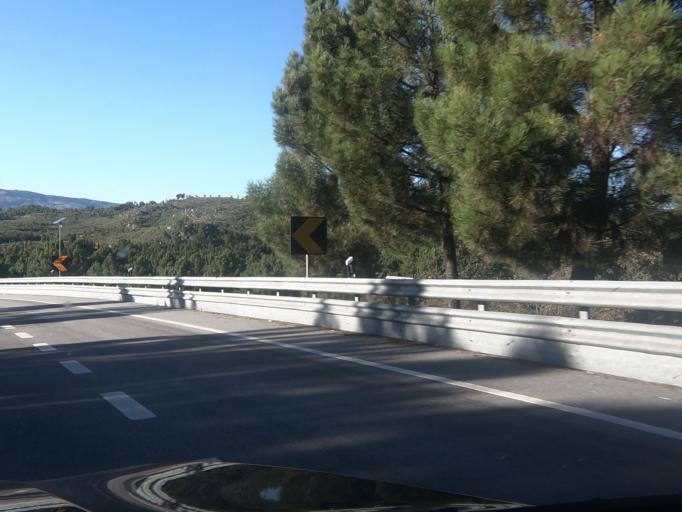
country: PT
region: Vila Real
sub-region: Vila Real
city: Vila Real
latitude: 41.3280
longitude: -7.6723
